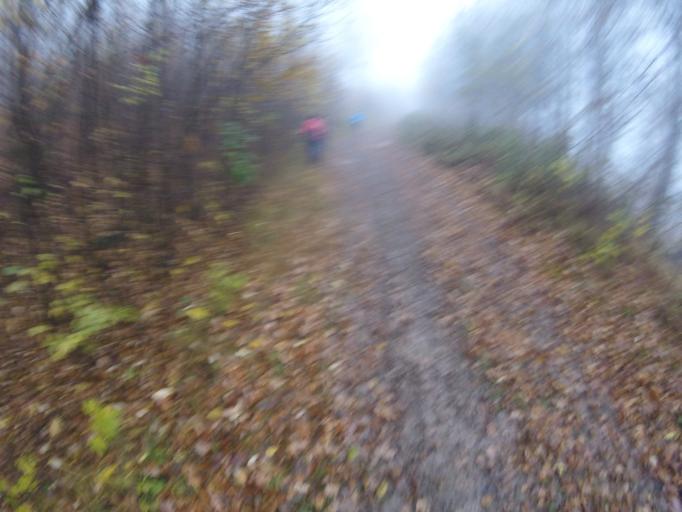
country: HU
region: Nograd
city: Rimoc
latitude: 47.9796
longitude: 19.5533
